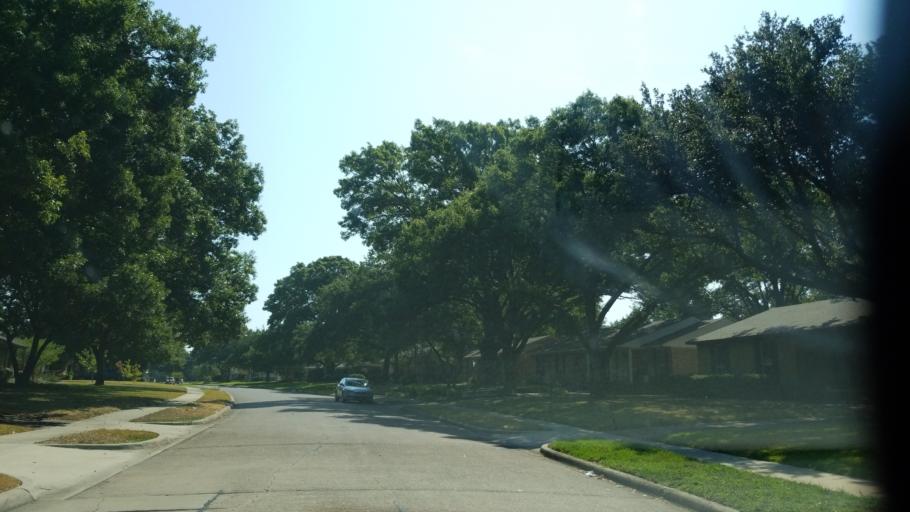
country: US
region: Texas
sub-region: Dallas County
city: Richardson
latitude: 32.9601
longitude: -96.7428
